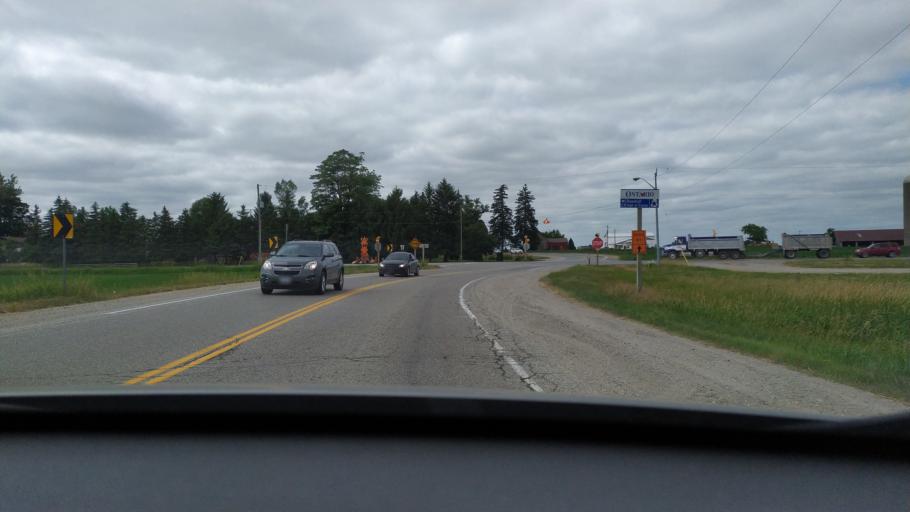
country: CA
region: Ontario
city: Stratford
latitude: 43.3156
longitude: -80.9842
